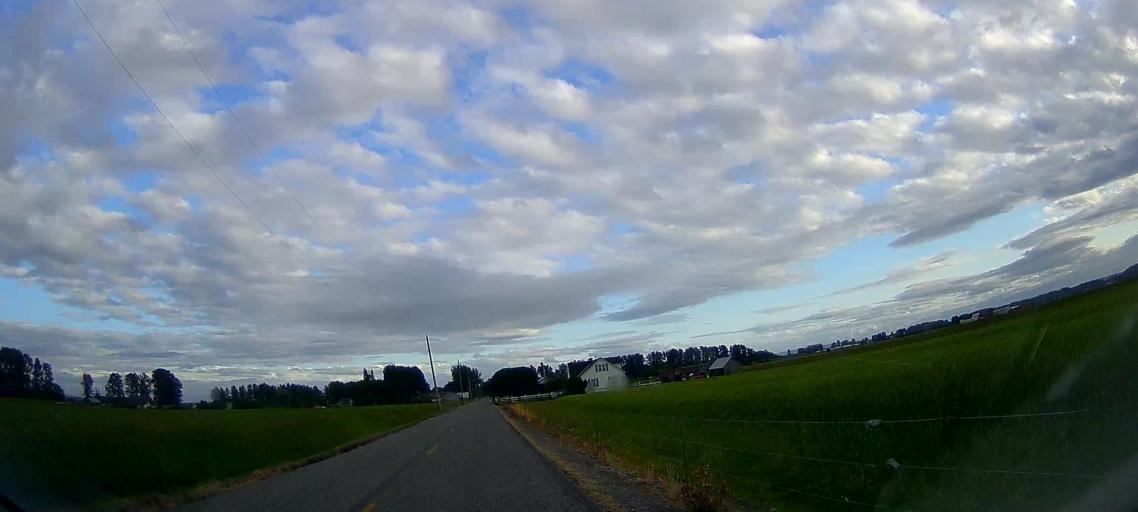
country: US
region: Washington
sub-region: Skagit County
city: Mount Vernon
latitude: 48.3925
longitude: -122.3843
